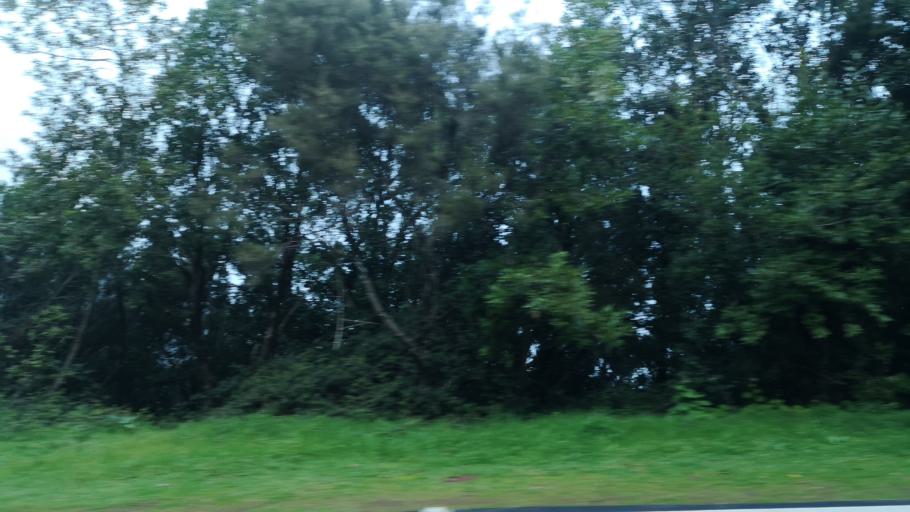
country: ES
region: Canary Islands
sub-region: Provincia de Santa Cruz de Tenerife
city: Alajero
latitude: 28.1120
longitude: -17.2416
